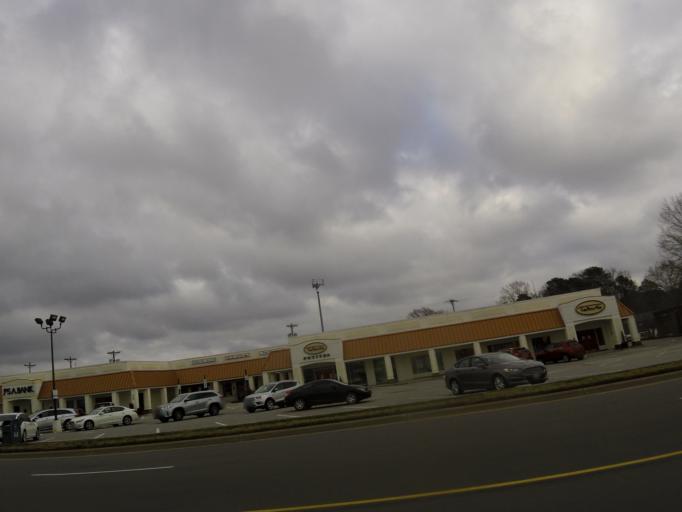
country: US
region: North Carolina
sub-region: Nash County
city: Rocky Mount
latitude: 35.9625
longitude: -77.8493
